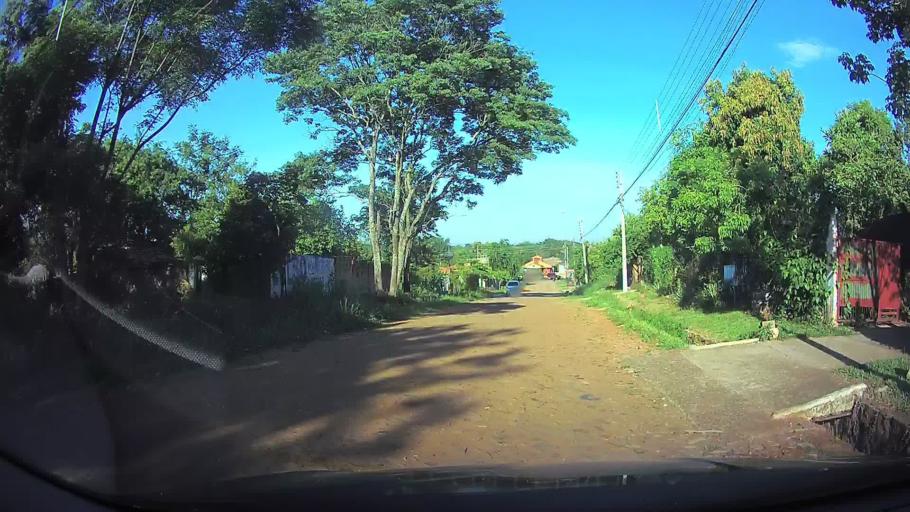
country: PY
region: Central
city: San Lorenzo
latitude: -25.2569
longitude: -57.4730
